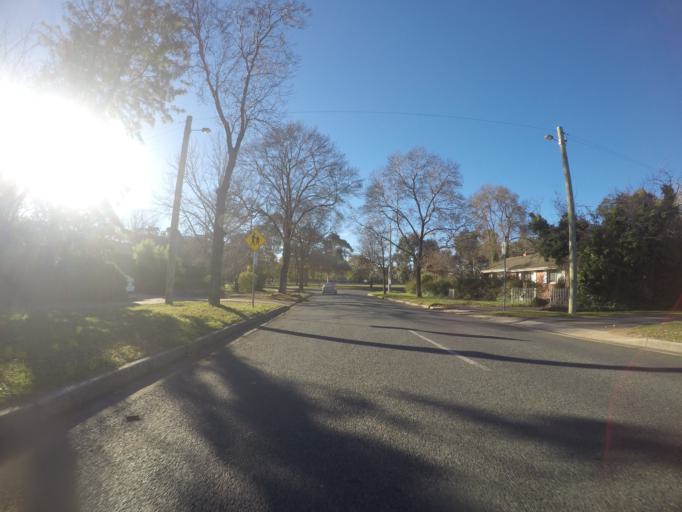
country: AU
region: Australian Capital Territory
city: Acton
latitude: -35.2543
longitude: 149.1354
